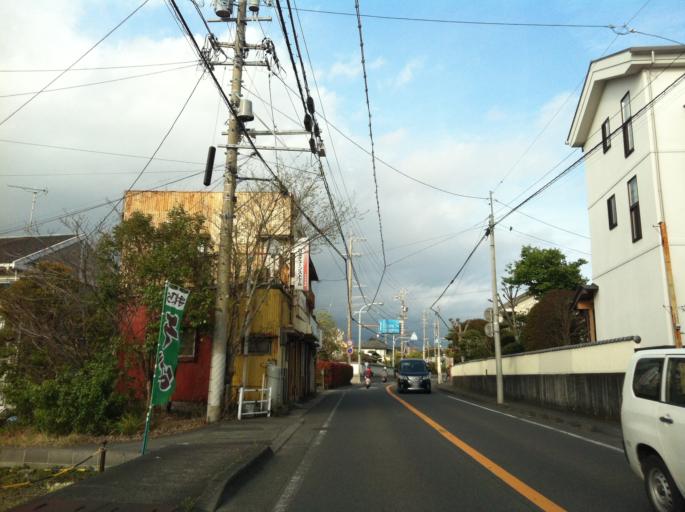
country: JP
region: Shizuoka
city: Shizuoka-shi
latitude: 34.9845
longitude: 138.4275
